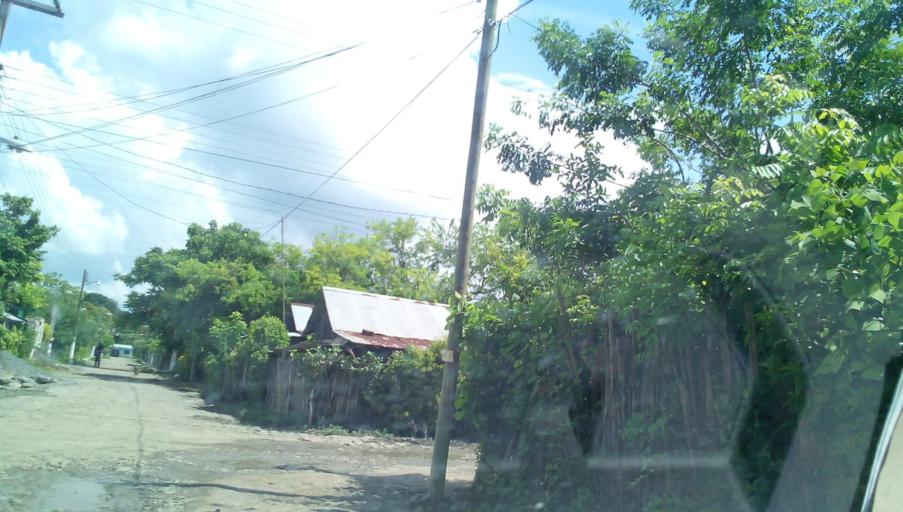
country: MX
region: Veracruz
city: Tamalin
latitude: 21.3680
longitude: -97.8000
